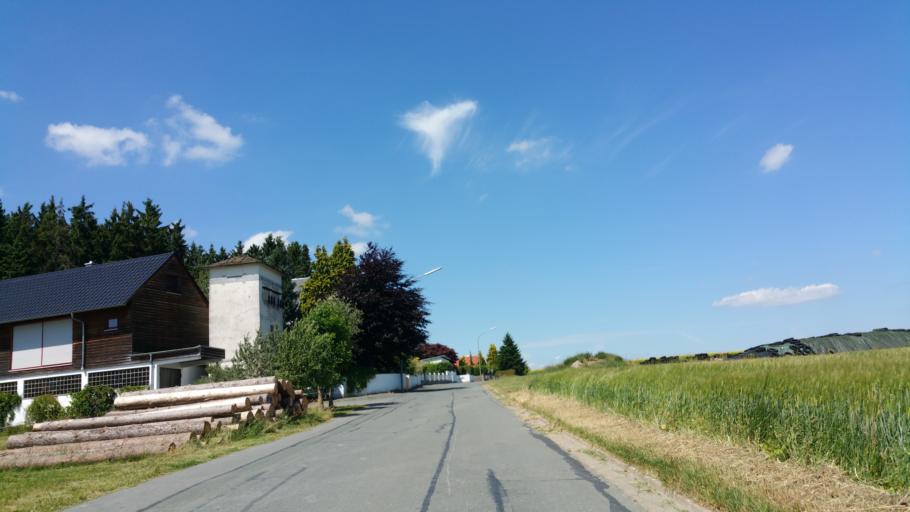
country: DE
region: Bavaria
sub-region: Upper Franconia
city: Koditz
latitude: 50.3568
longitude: 11.8561
